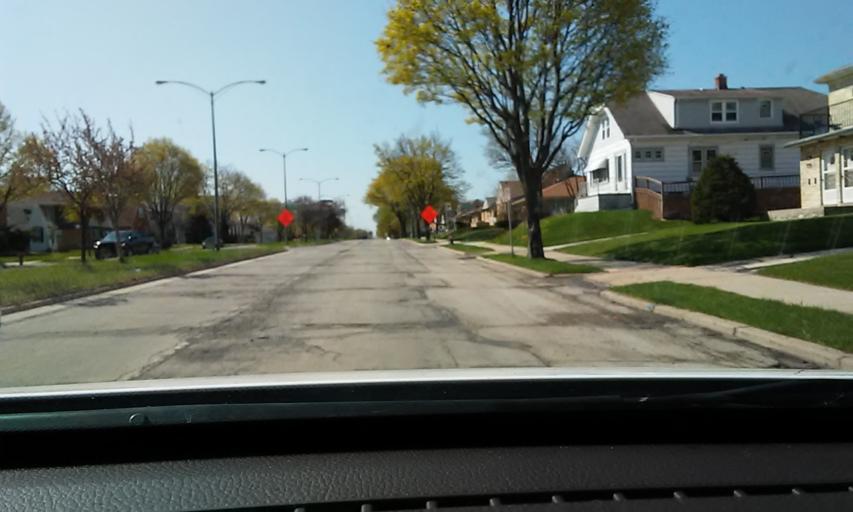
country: US
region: Wisconsin
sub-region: Milwaukee County
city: West Milwaukee
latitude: 42.9943
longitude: -87.9878
